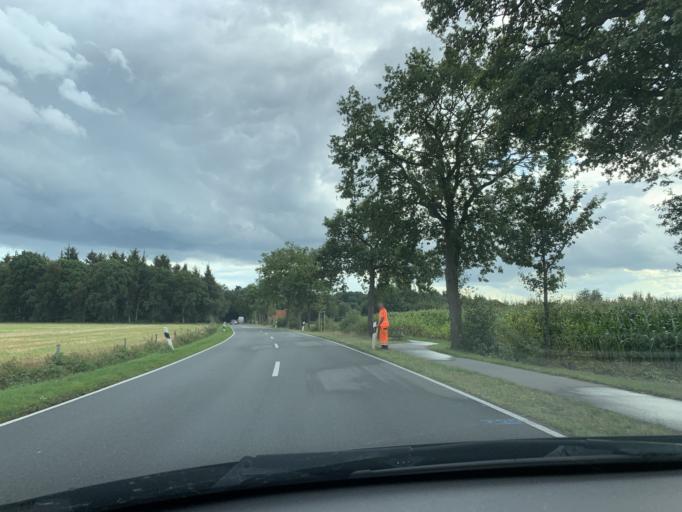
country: DE
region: Lower Saxony
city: Westerstede
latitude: 53.3040
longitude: 7.9157
